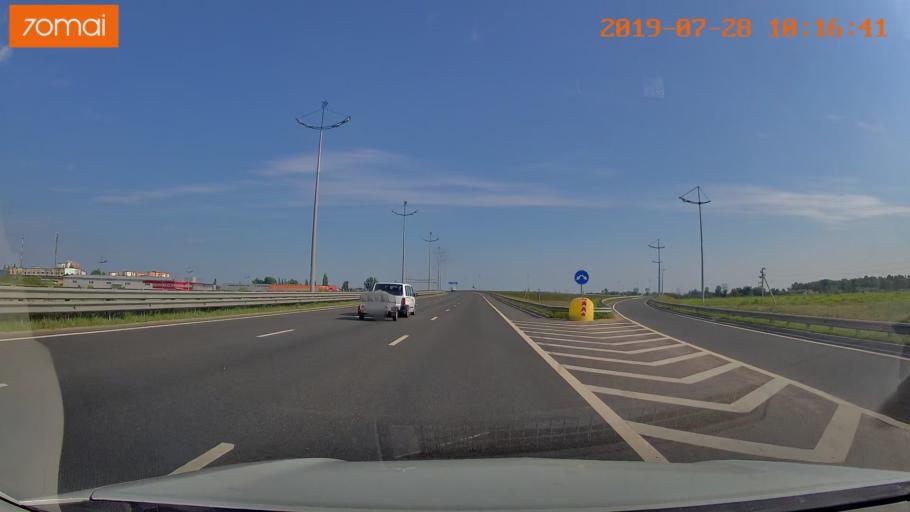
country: RU
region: Kaliningrad
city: Bol'shoe Isakovo
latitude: 54.7293
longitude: 20.5976
